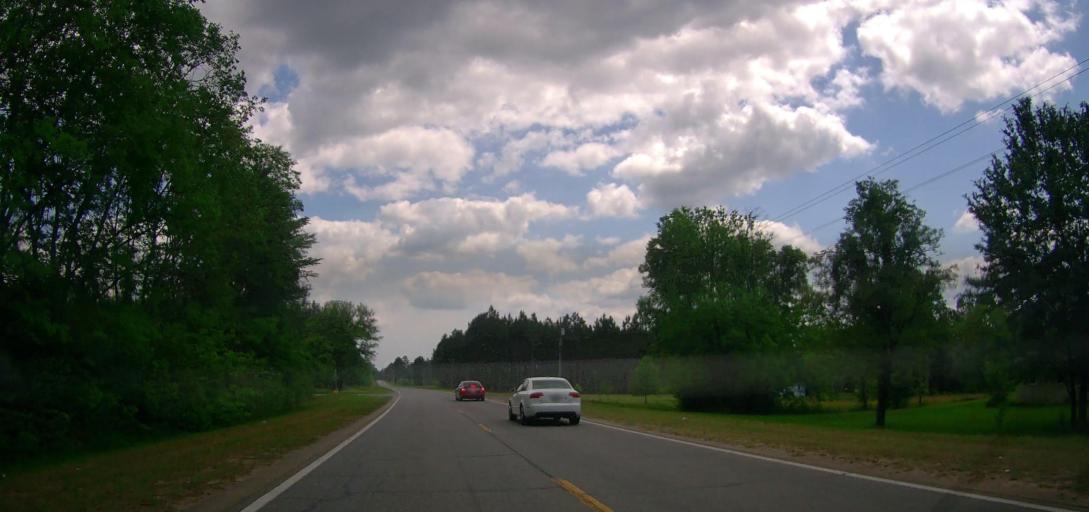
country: US
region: Georgia
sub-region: Laurens County
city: East Dublin
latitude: 32.4999
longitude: -82.8328
